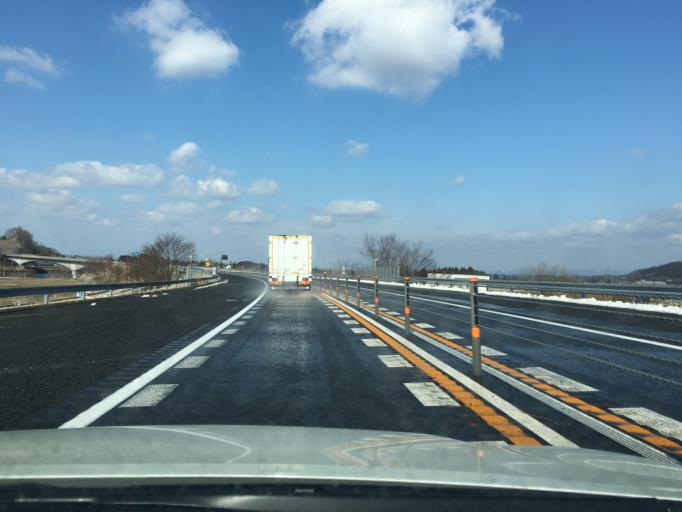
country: JP
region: Yamagata
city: Tsuruoka
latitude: 38.6181
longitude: 139.8436
